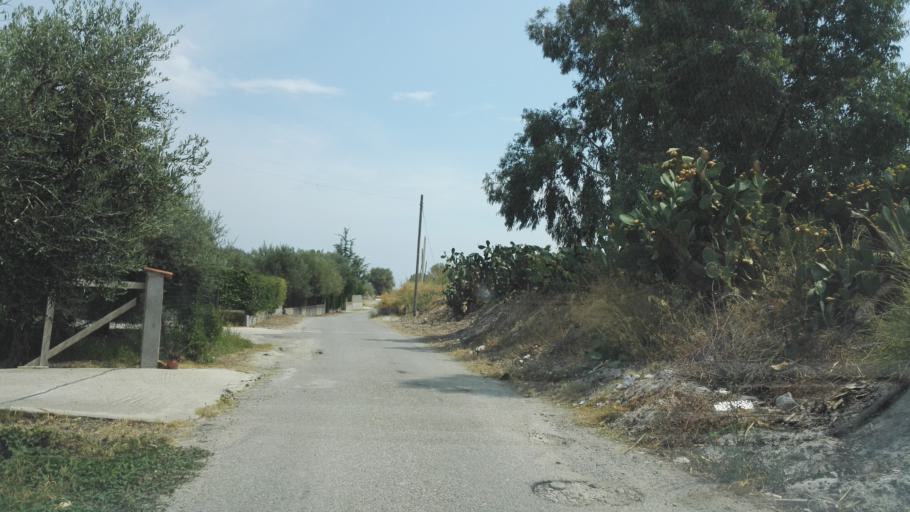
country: IT
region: Calabria
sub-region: Provincia di Reggio Calabria
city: Monasterace Marina
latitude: 38.4314
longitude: 16.5566
